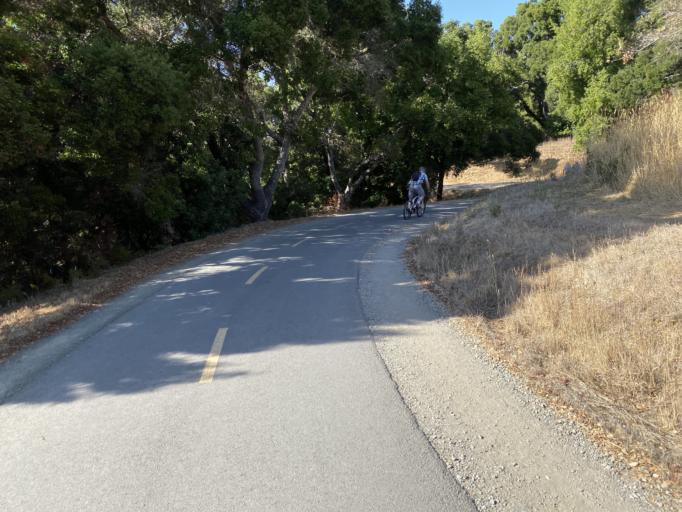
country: US
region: California
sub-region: San Mateo County
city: Hillsborough
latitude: 37.5432
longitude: -122.3778
